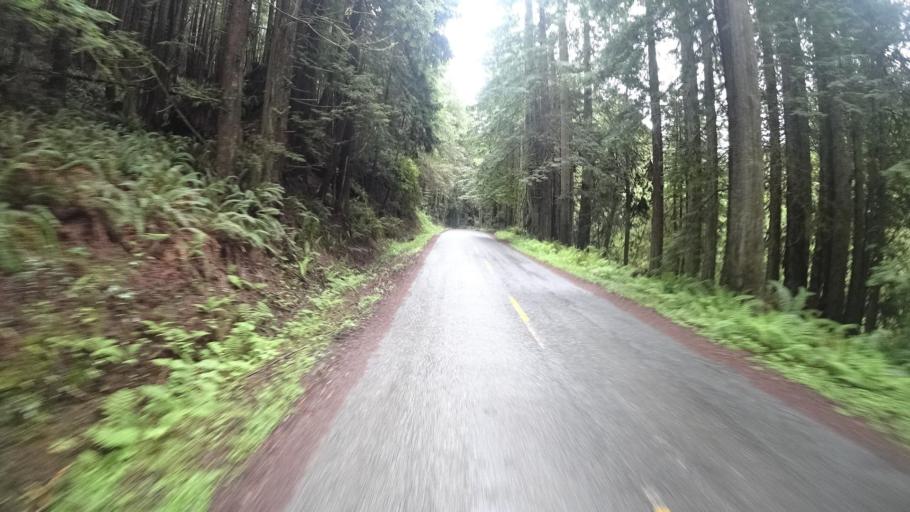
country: US
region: California
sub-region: Humboldt County
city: Bayside
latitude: 40.8214
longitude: -124.0314
